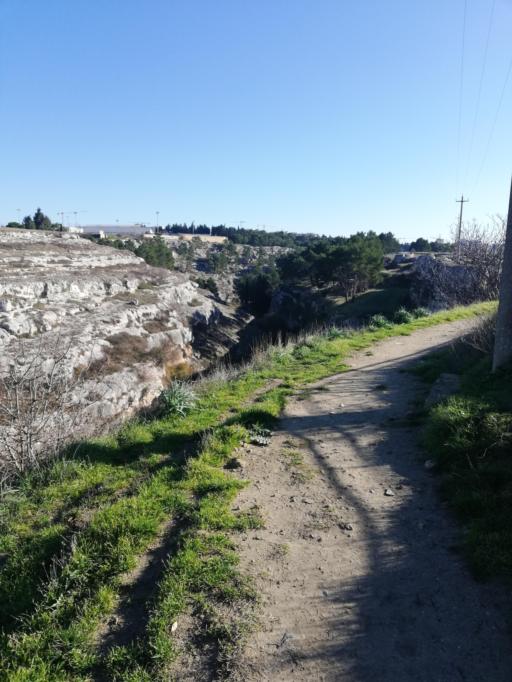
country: IT
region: Apulia
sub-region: Provincia di Bari
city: Gravina in Puglia
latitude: 40.8246
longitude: 16.4056
